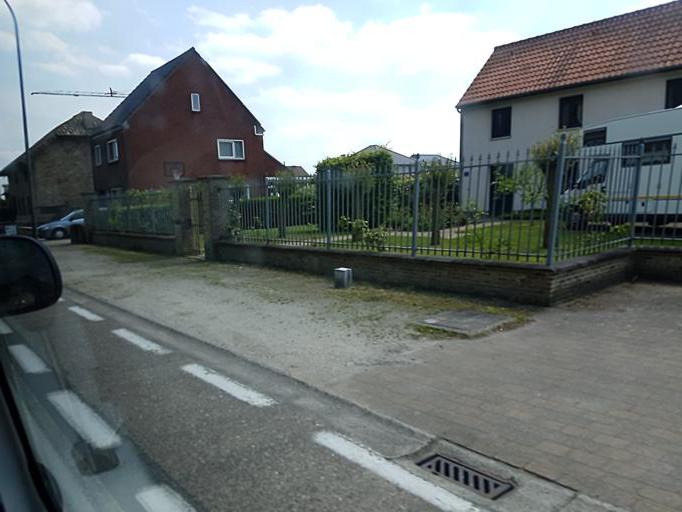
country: BE
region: Flanders
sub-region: Provincie Limburg
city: Neerpelt
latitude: 51.2314
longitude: 5.4542
